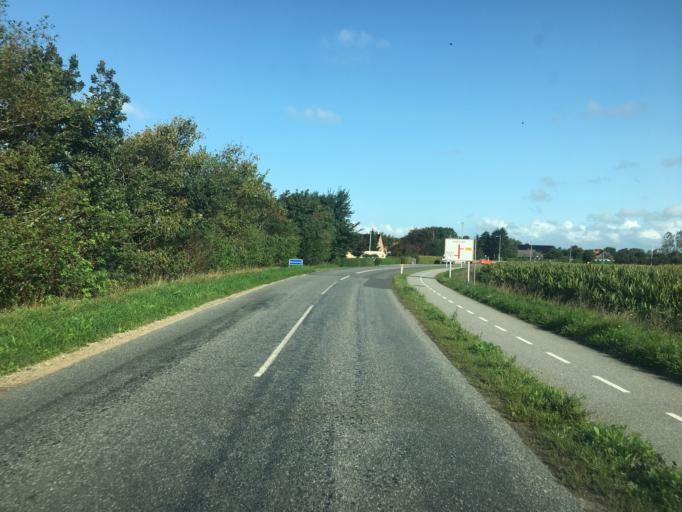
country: DK
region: South Denmark
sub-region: Tonder Kommune
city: Sherrebek
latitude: 55.1482
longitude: 8.7554
